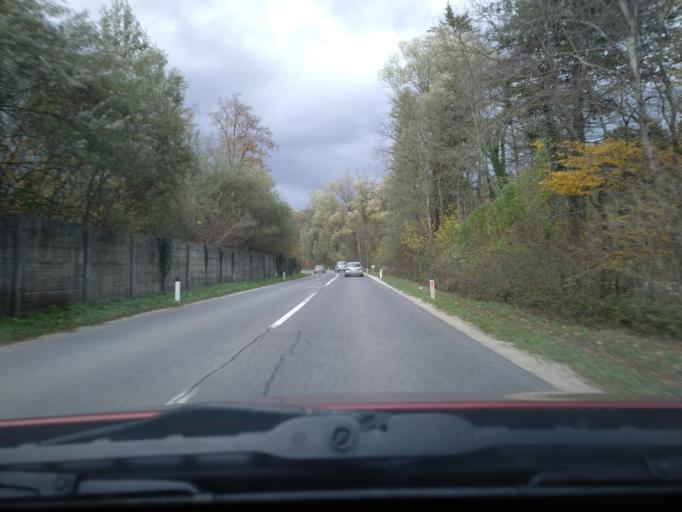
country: SI
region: Kamnik
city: Mekinje
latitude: 46.2422
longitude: 14.6047
